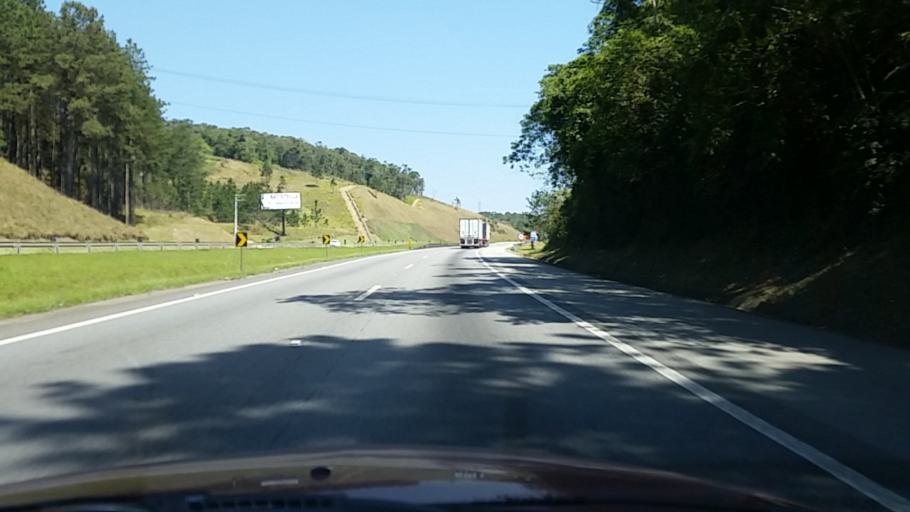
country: BR
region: Sao Paulo
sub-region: Juquitiba
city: Juquitiba
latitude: -23.9719
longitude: -47.1359
